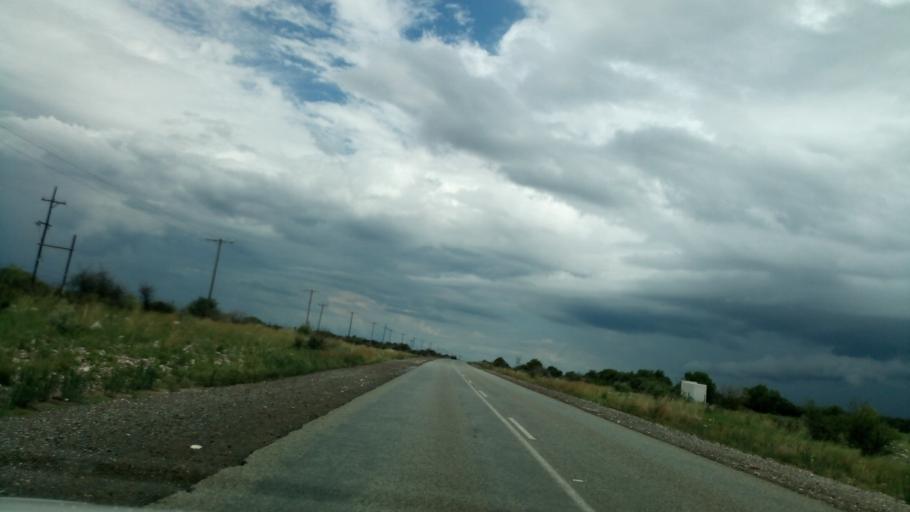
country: ZA
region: Northern Cape
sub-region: Siyanda District Municipality
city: Danielskuil
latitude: -28.2582
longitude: 24.0538
